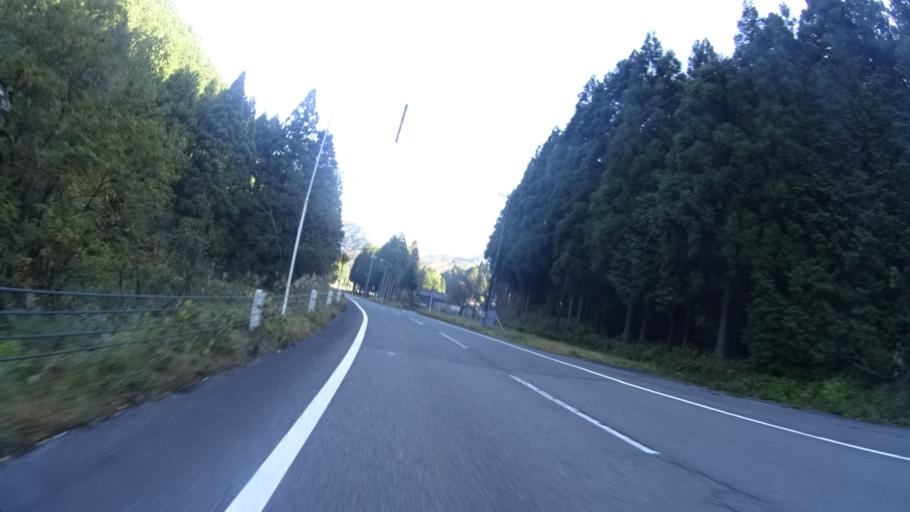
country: JP
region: Fukui
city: Maruoka
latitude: 36.1520
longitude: 136.3310
